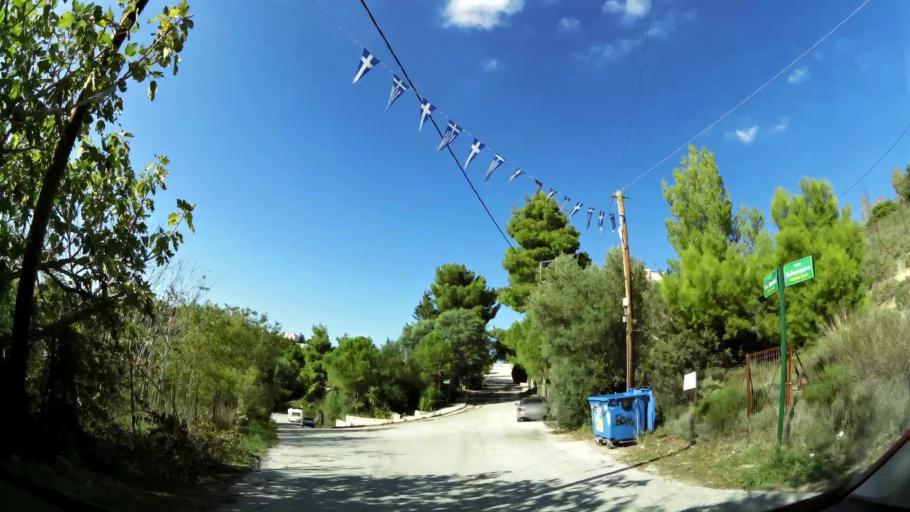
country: GR
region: Attica
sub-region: Nomarchia Anatolikis Attikis
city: Anthousa
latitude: 38.0189
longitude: 23.8781
